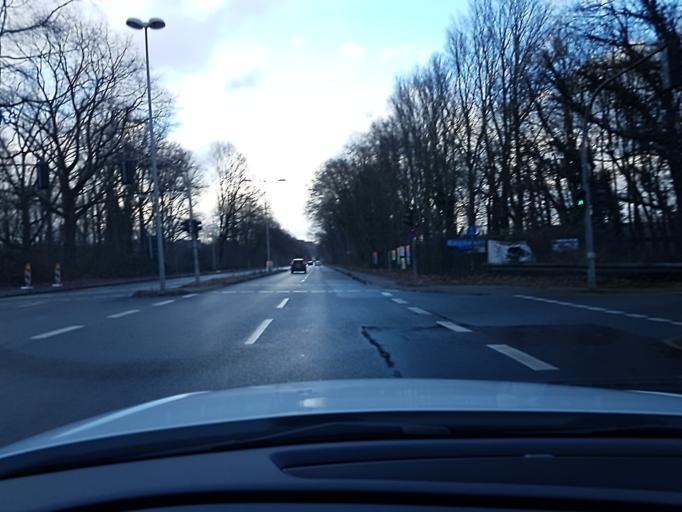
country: DE
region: North Rhine-Westphalia
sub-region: Regierungsbezirk Dusseldorf
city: Muelheim (Ruhr)
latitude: 51.4043
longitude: 6.8828
